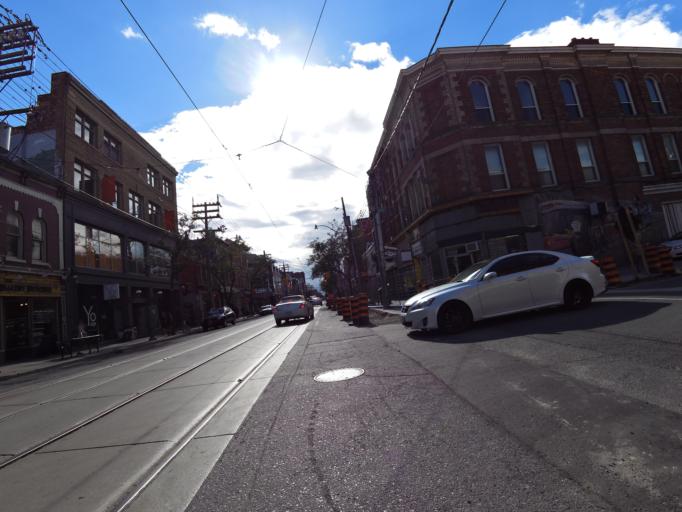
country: CA
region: Ontario
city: Toronto
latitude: 43.6479
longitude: -79.4005
